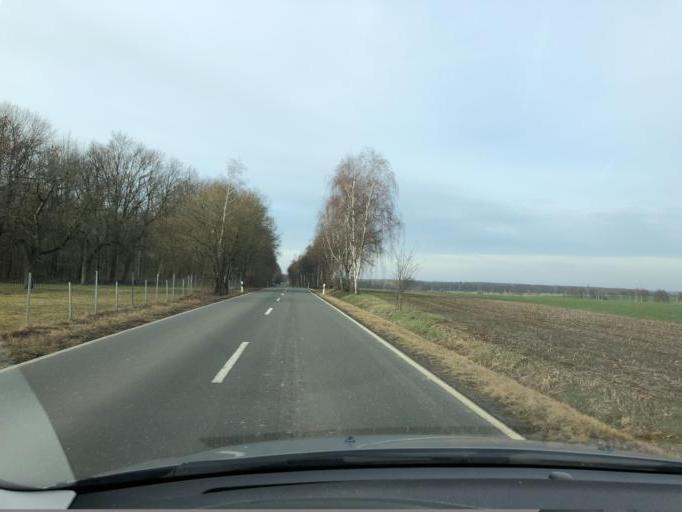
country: DE
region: Thuringia
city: Rastenberg
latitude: 51.1821
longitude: 11.4997
